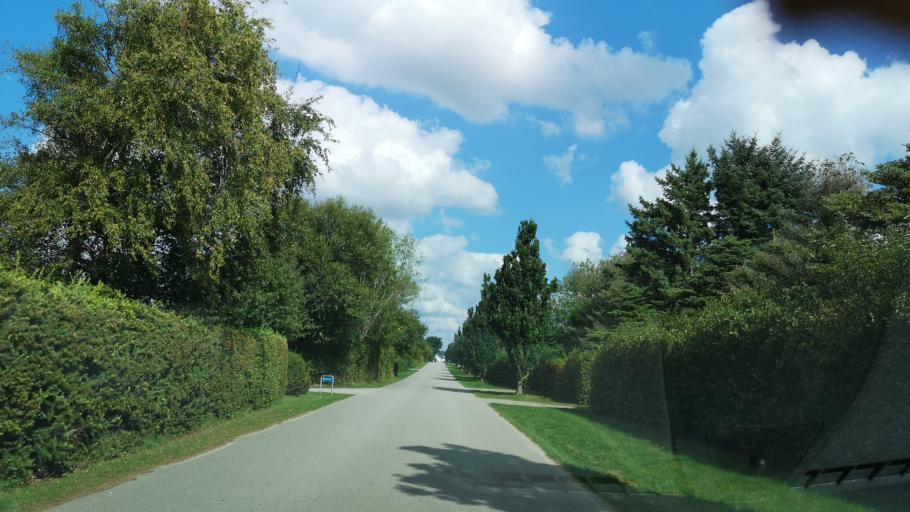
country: DK
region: Central Jutland
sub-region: Ringkobing-Skjern Kommune
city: Skjern
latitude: 55.8880
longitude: 8.3590
